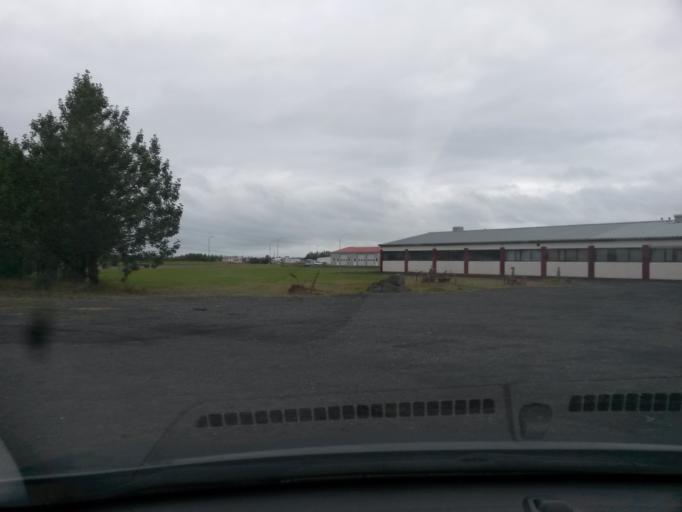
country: IS
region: South
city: Vestmannaeyjar
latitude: 63.7506
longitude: -20.2244
